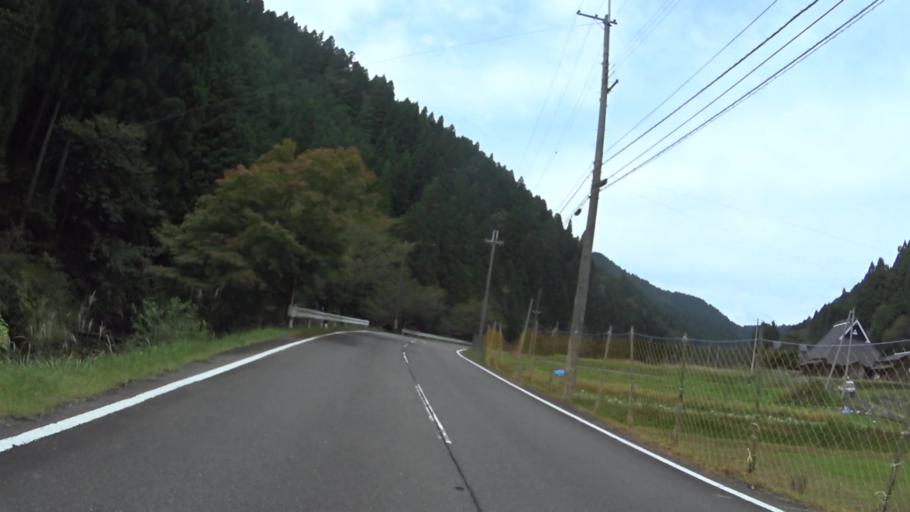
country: JP
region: Shiga Prefecture
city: Kitahama
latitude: 35.2620
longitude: 135.7515
